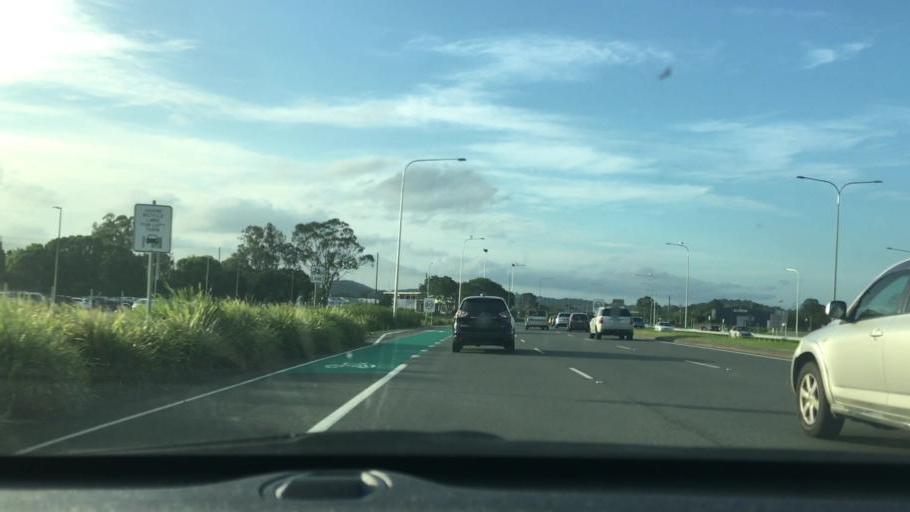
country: AU
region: Queensland
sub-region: Gold Coast
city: Nerang
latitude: -28.0056
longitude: 153.3634
